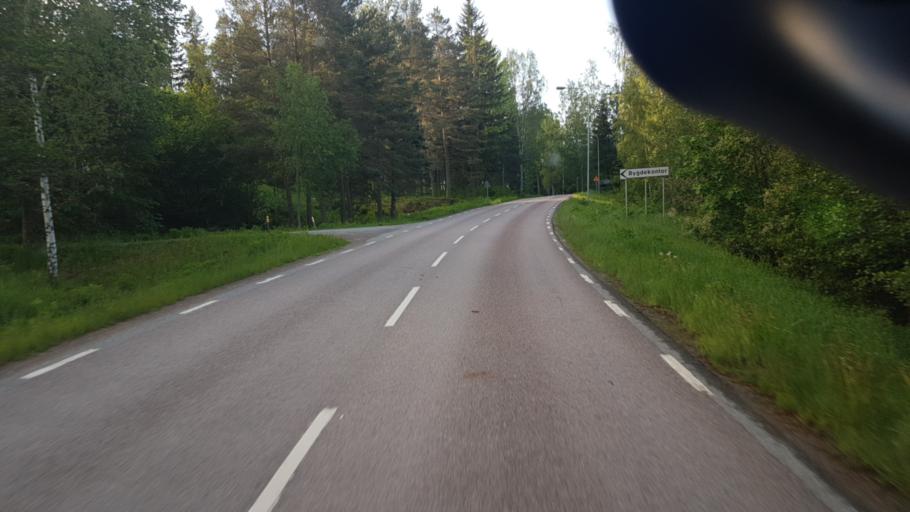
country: SE
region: Vaermland
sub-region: Arvika Kommun
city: Arvika
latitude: 59.5589
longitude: 12.5594
